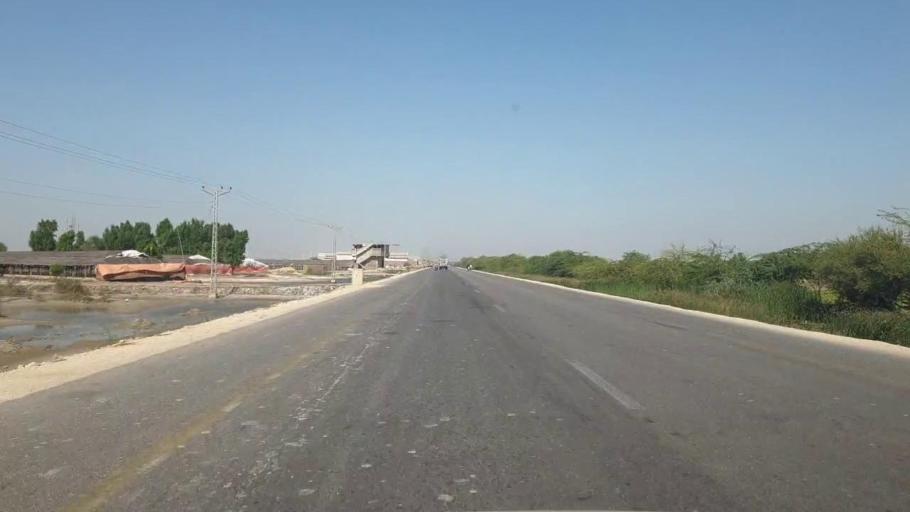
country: PK
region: Sindh
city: Talhar
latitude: 24.8609
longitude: 68.8166
